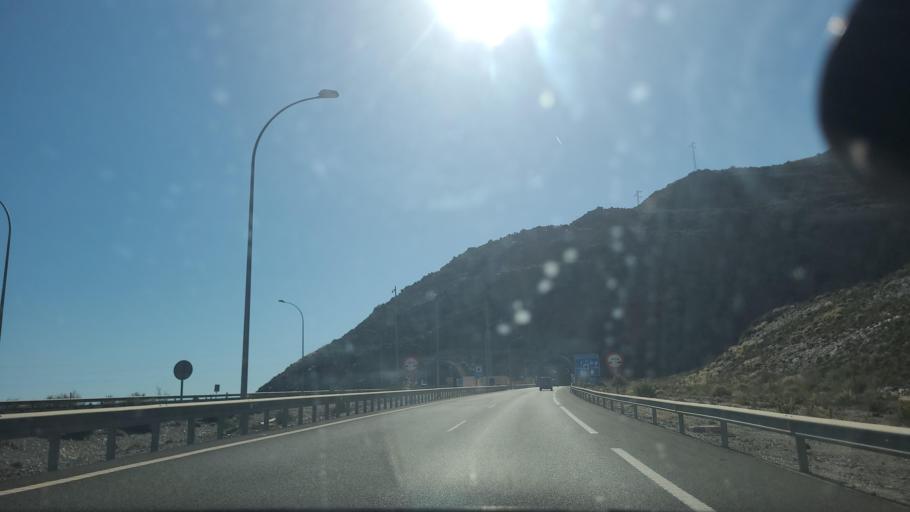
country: ES
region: Andalusia
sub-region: Provincia de Granada
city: Sorvilan
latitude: 36.7571
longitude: -3.2448
